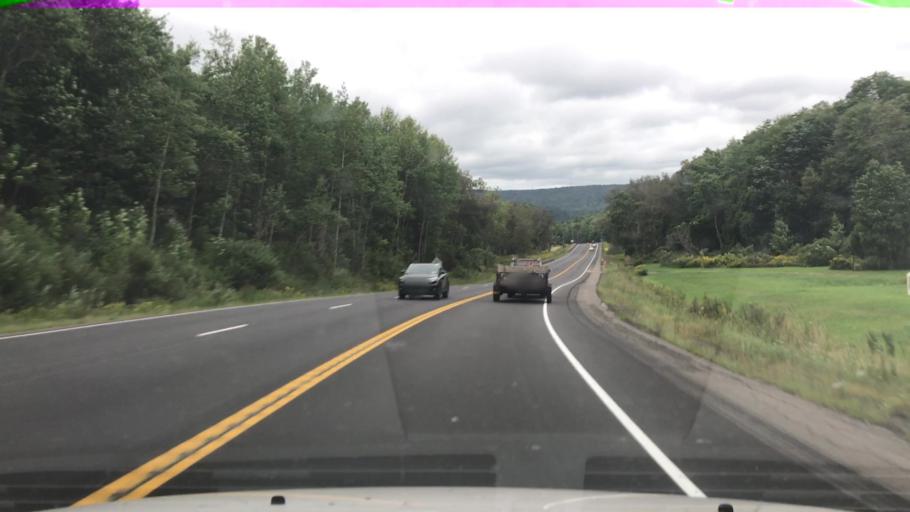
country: US
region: New York
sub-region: Cattaraugus County
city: Little Valley
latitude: 42.3366
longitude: -78.6601
